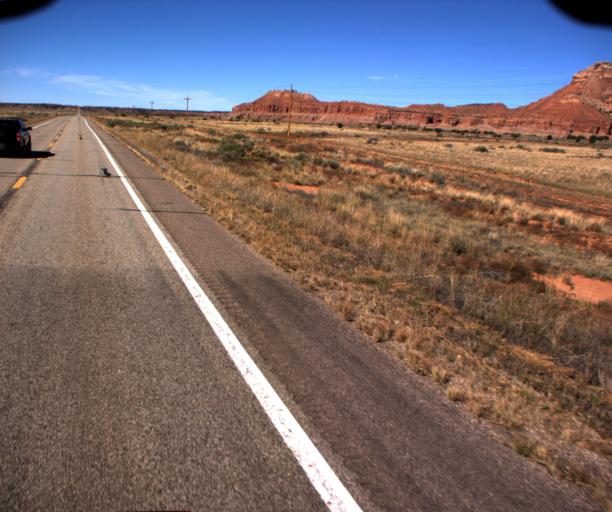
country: US
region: Arizona
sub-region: Mohave County
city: Colorado City
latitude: 36.8657
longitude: -112.8367
